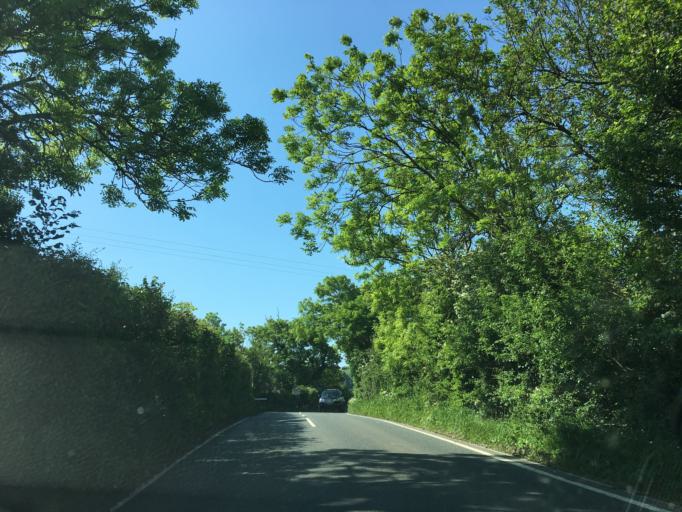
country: GB
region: England
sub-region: Isle of Wight
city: Brading
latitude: 50.6930
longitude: -1.1774
